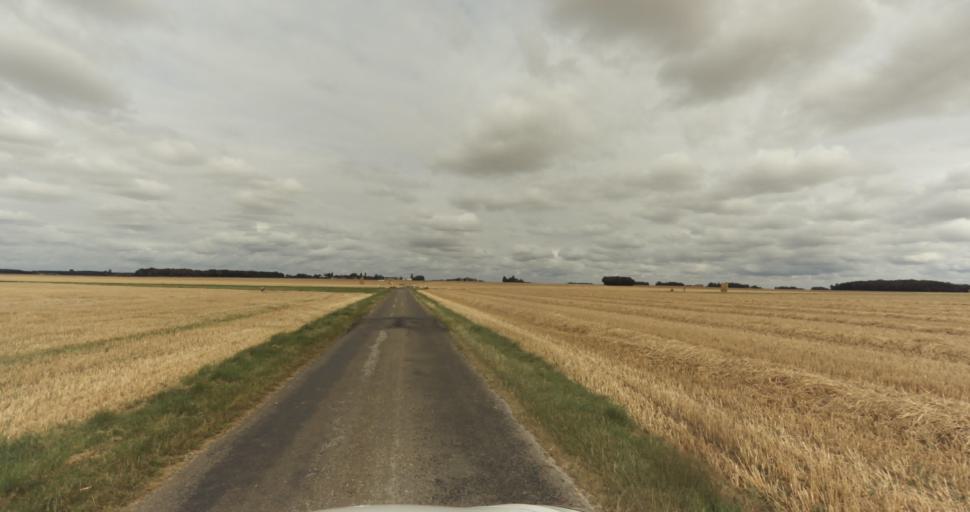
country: FR
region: Haute-Normandie
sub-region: Departement de l'Eure
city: Tillieres-sur-Avre
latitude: 48.7798
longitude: 1.0760
